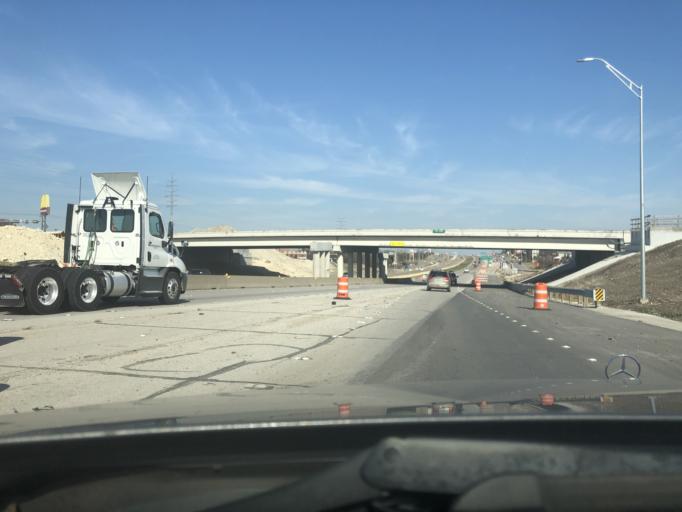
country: US
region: Texas
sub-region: Dallas County
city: Cedar Hill
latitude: 32.5949
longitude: -96.9407
